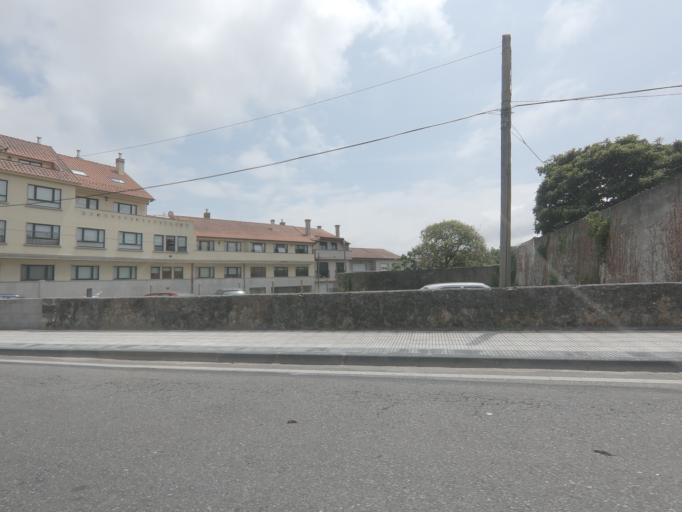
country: ES
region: Galicia
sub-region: Provincia de Pontevedra
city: A Guarda
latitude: 41.9056
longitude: -8.8637
